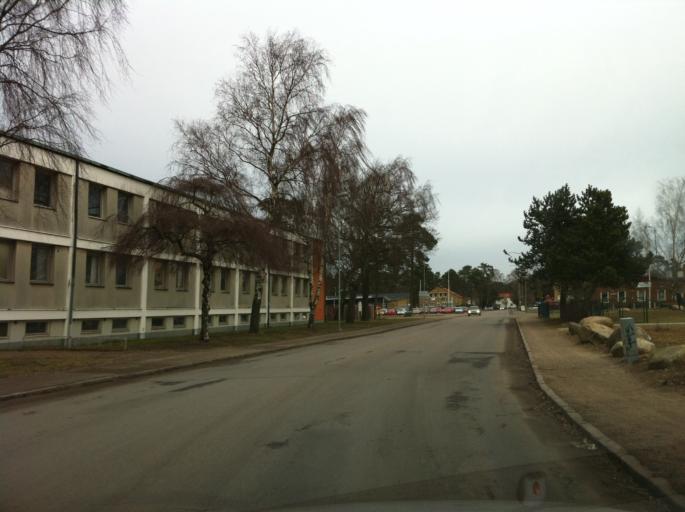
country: SE
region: Skane
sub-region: Angelholms Kommun
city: AEngelholm
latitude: 56.2484
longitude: 12.8545
